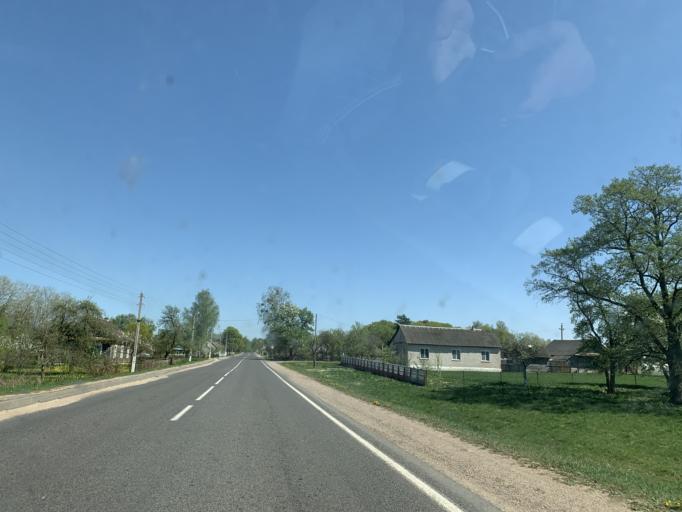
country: BY
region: Minsk
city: Kapyl'
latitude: 53.2574
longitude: 26.9490
